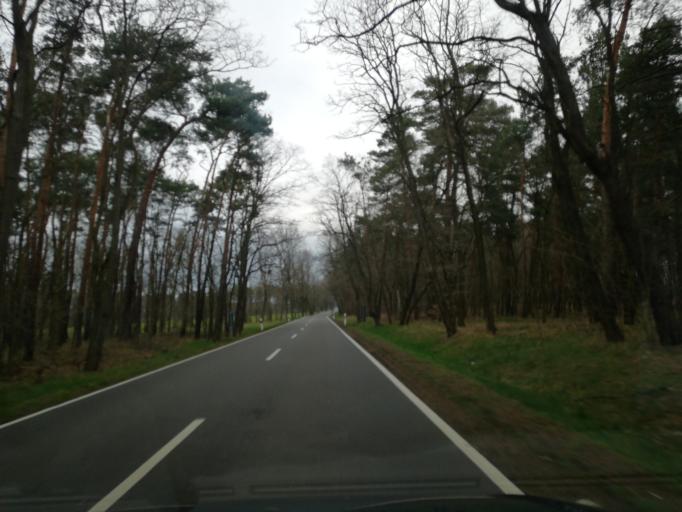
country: DE
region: Brandenburg
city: Vetschau
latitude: 51.7454
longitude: 14.0522
